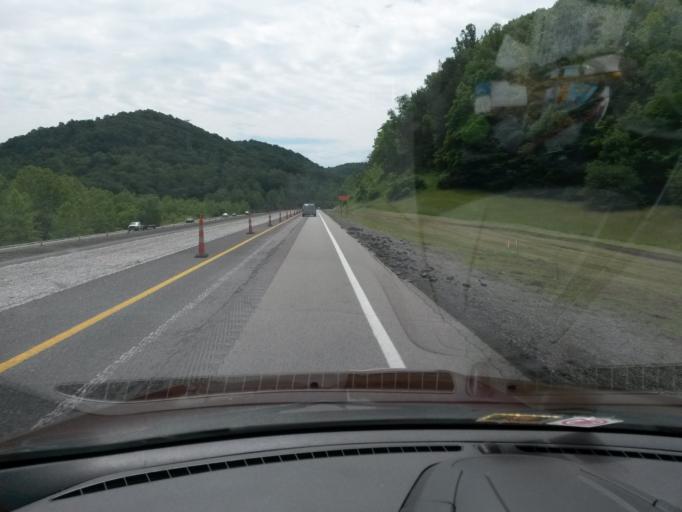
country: US
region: West Virginia
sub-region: Braxton County
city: Sutton
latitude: 38.7568
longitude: -80.6790
